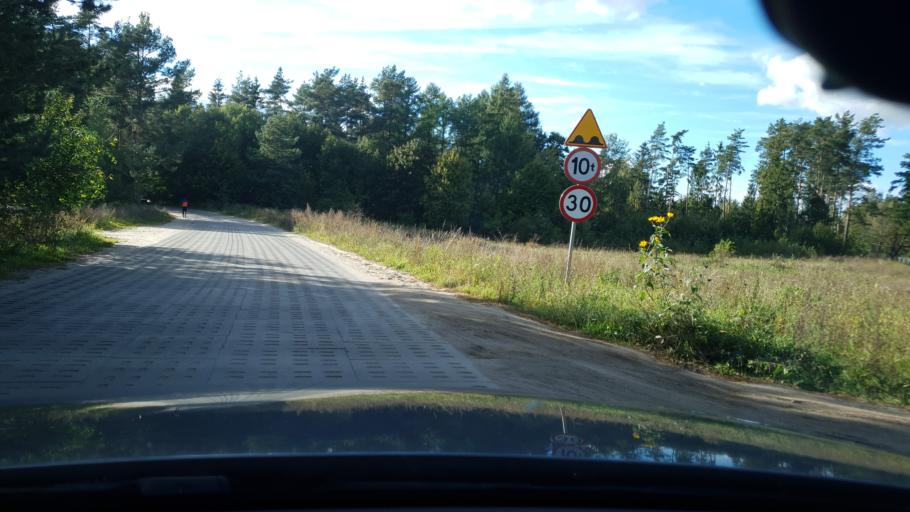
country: PL
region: Pomeranian Voivodeship
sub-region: Powiat kartuski
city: Chwaszczyno
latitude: 54.4821
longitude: 18.4268
